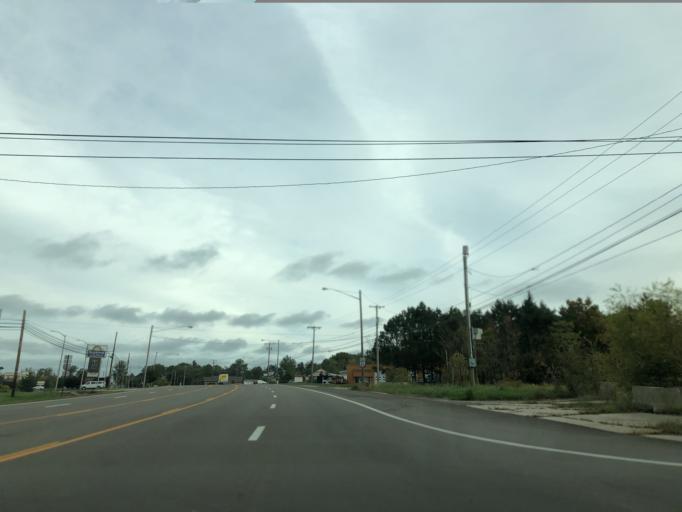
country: US
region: Ohio
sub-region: Summit County
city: Richfield
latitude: 41.2622
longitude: -81.6294
